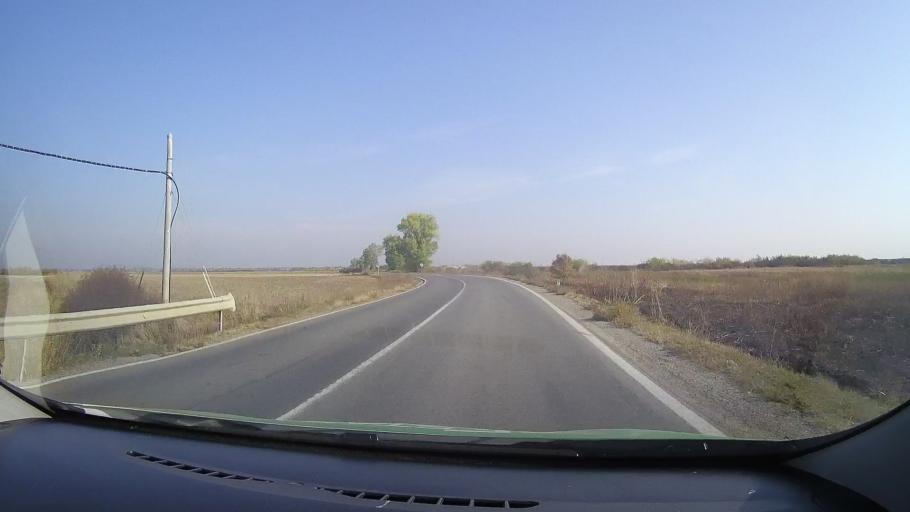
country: RO
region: Arad
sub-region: Comuna Pilu
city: Pilu
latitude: 46.5975
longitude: 21.3490
